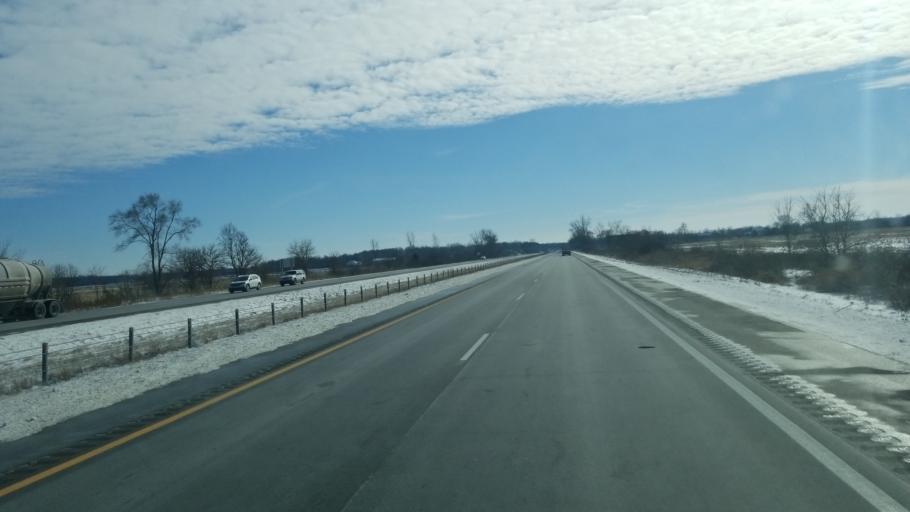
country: US
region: Michigan
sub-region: Washtenaw County
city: Milan
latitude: 42.0686
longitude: -83.6707
